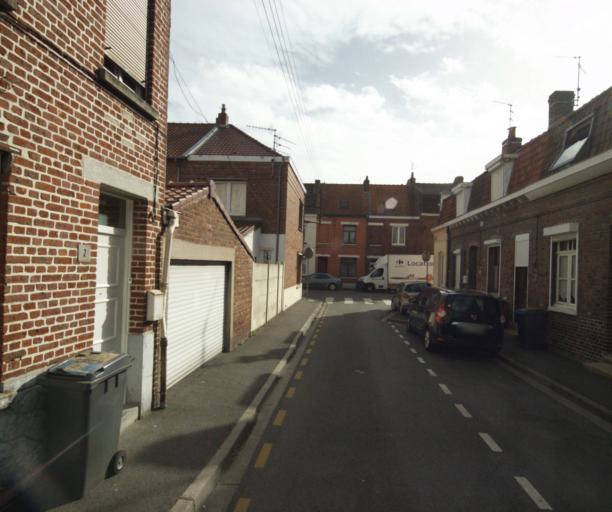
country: FR
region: Nord-Pas-de-Calais
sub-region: Departement du Nord
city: La Bassee
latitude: 50.5299
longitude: 2.8006
